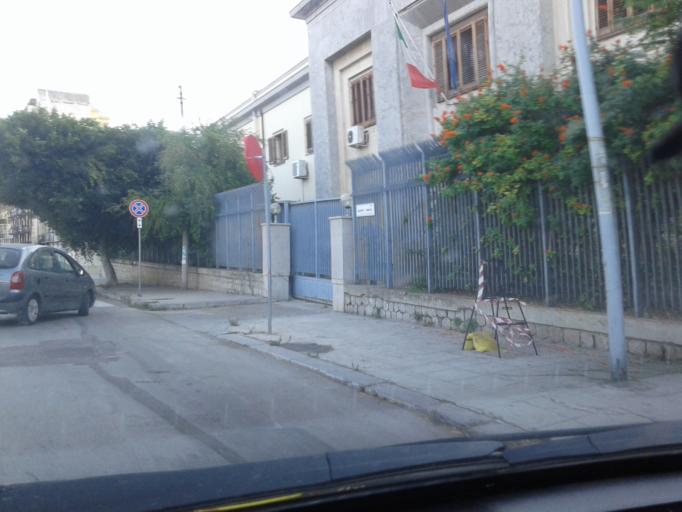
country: IT
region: Sicily
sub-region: Palermo
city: Palermo
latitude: 38.1031
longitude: 13.3406
